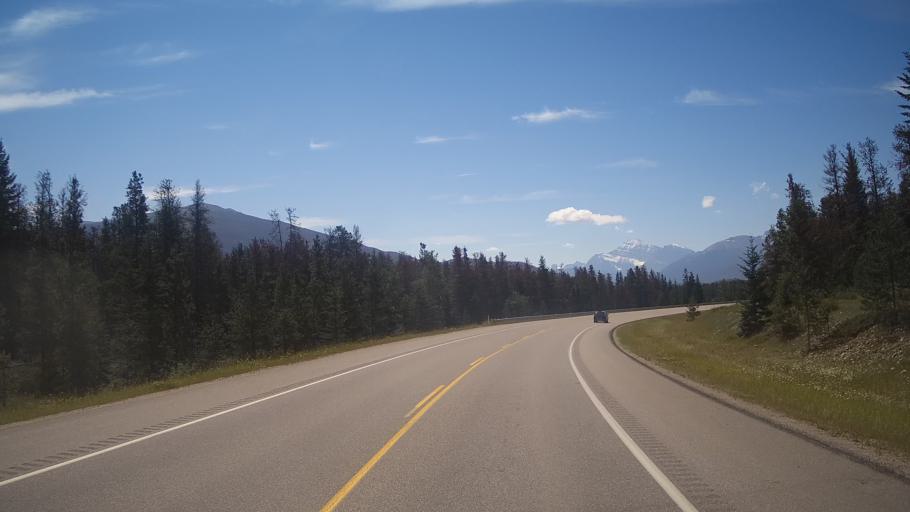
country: CA
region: Alberta
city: Jasper Park Lodge
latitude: 52.9304
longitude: -118.0376
